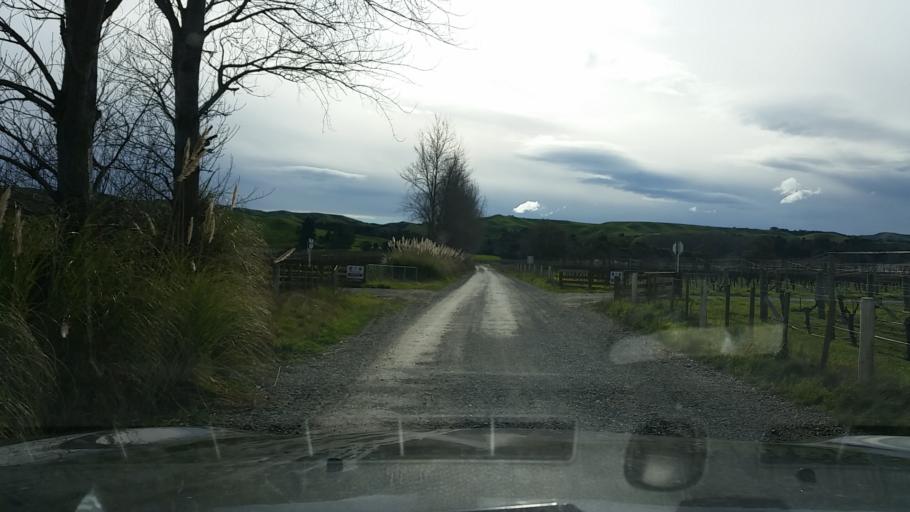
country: NZ
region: Marlborough
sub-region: Marlborough District
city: Blenheim
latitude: -41.6229
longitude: 174.0995
